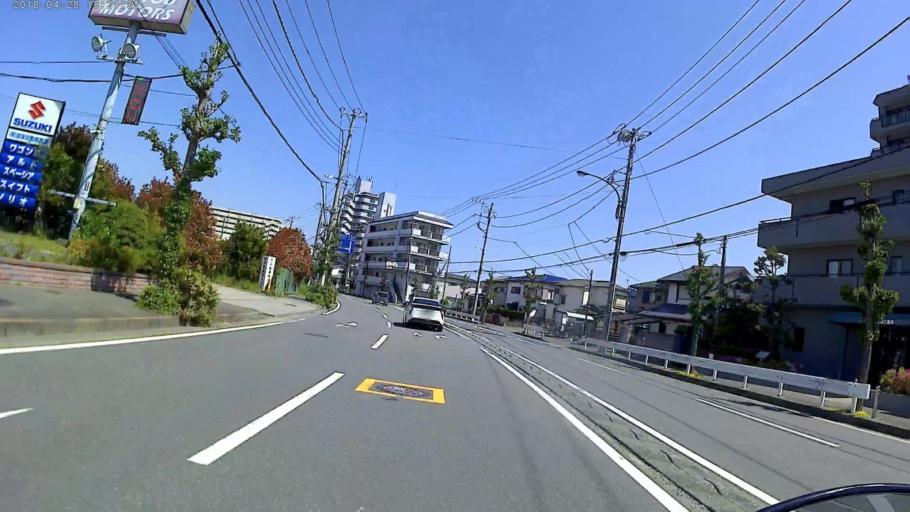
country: JP
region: Kanagawa
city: Yokosuka
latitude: 35.2324
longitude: 139.6959
